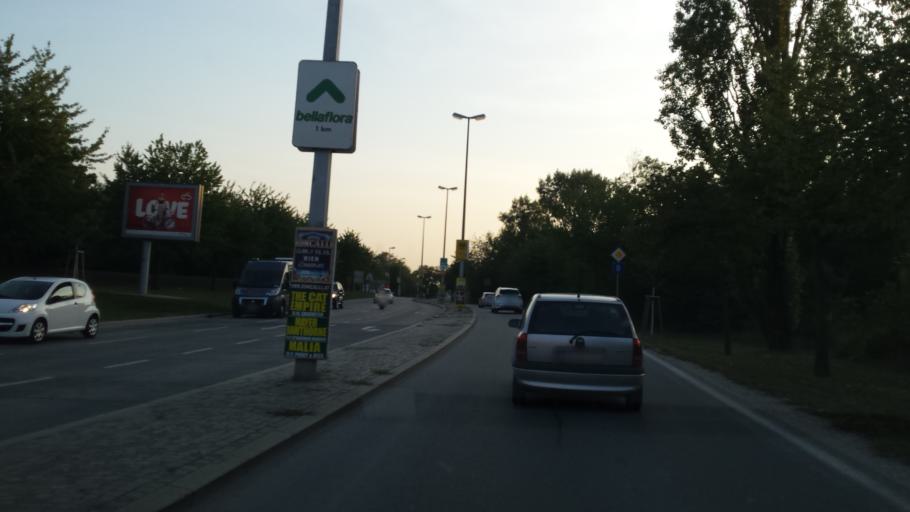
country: AT
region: Lower Austria
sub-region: Politischer Bezirk Wien-Umgebung
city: Gerasdorf bei Wien
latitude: 48.2746
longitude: 16.4726
